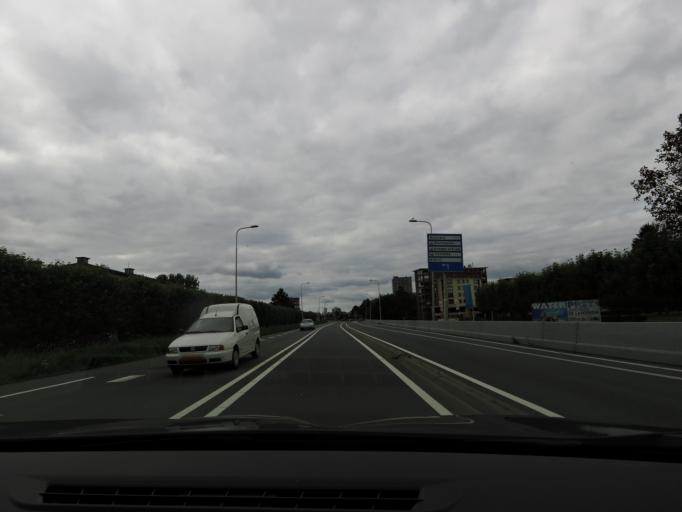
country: NL
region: South Holland
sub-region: Gemeente Krimpen aan den IJssel
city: Krimpen aan den IJssel
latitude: 51.9100
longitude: 4.5923
